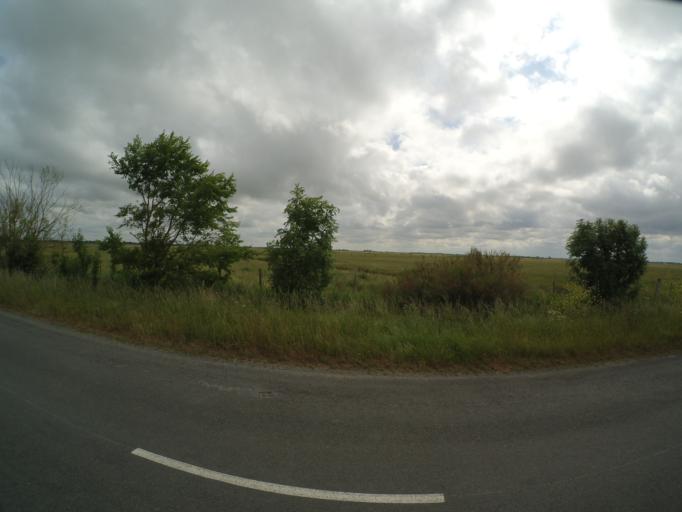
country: FR
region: Poitou-Charentes
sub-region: Departement de la Charente-Maritime
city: Yves
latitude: 46.0268
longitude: -1.0477
